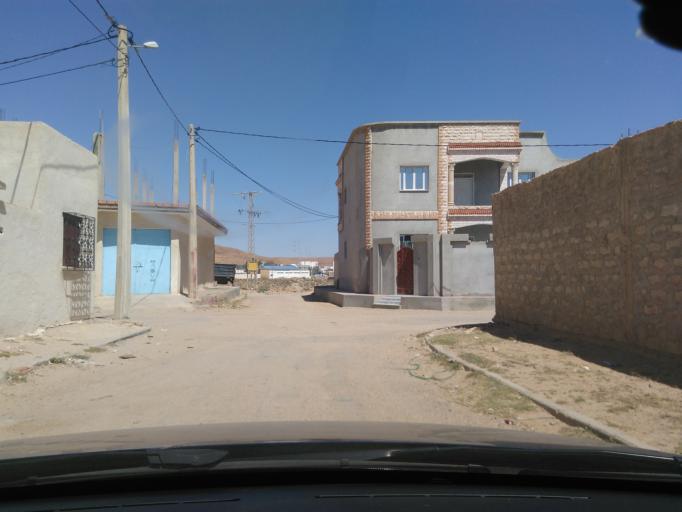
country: TN
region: Tataouine
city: Tataouine
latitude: 32.9455
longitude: 10.4607
